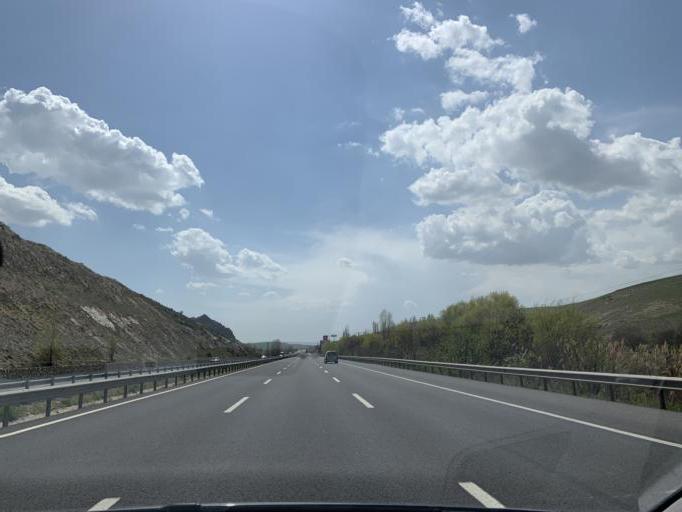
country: TR
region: Ankara
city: Temelli
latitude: 39.7823
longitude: 32.5106
